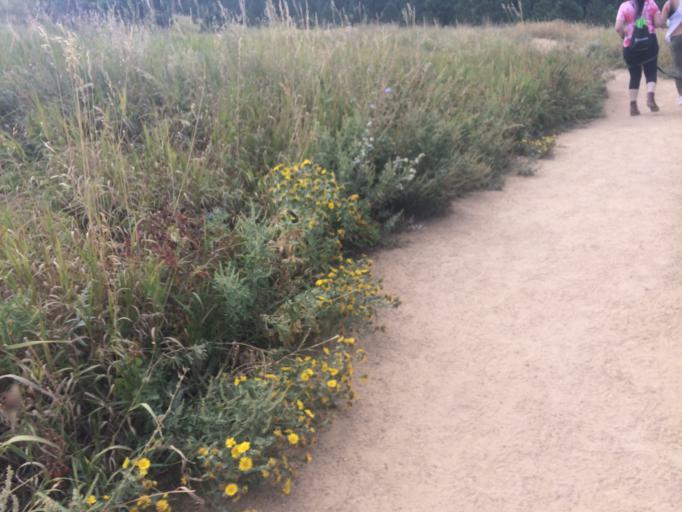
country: US
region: Colorado
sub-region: Boulder County
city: Boulder
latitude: 39.9990
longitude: -105.2895
